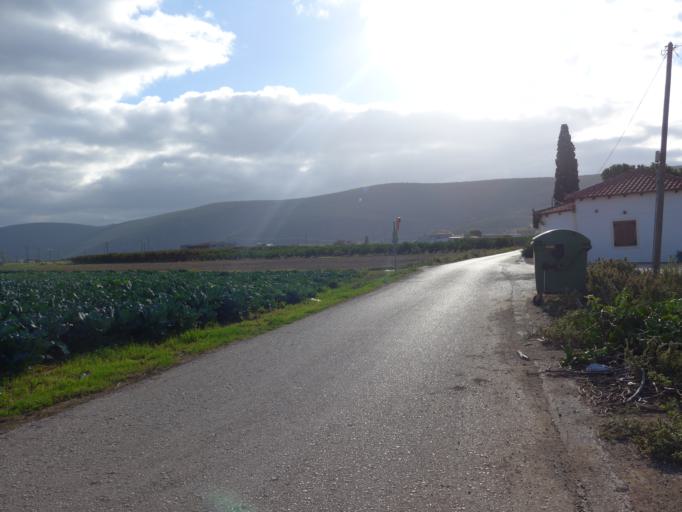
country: GR
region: Peloponnese
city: Asklipieio
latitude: 37.4923
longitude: 23.0058
